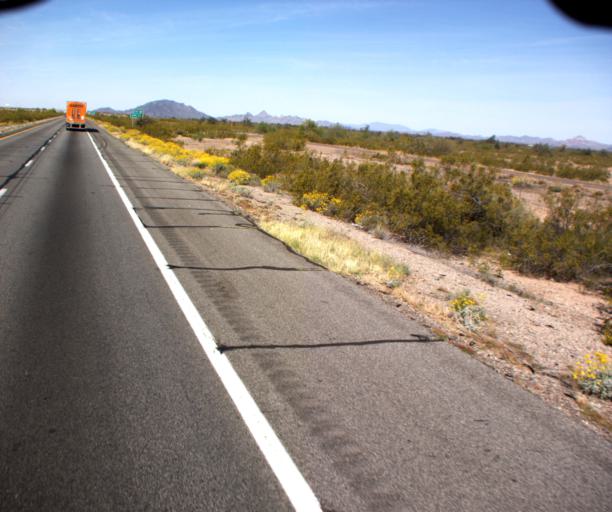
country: US
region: Arizona
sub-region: Maricopa County
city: Buckeye
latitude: 33.4945
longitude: -112.9233
